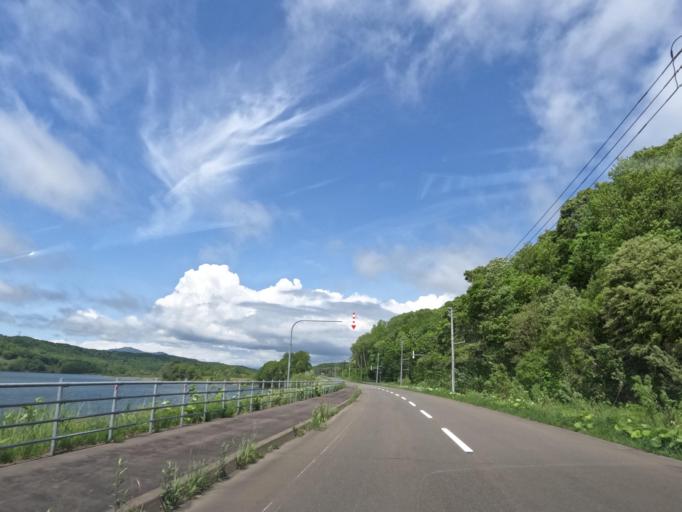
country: JP
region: Hokkaido
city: Tobetsu
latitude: 43.3635
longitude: 141.5714
